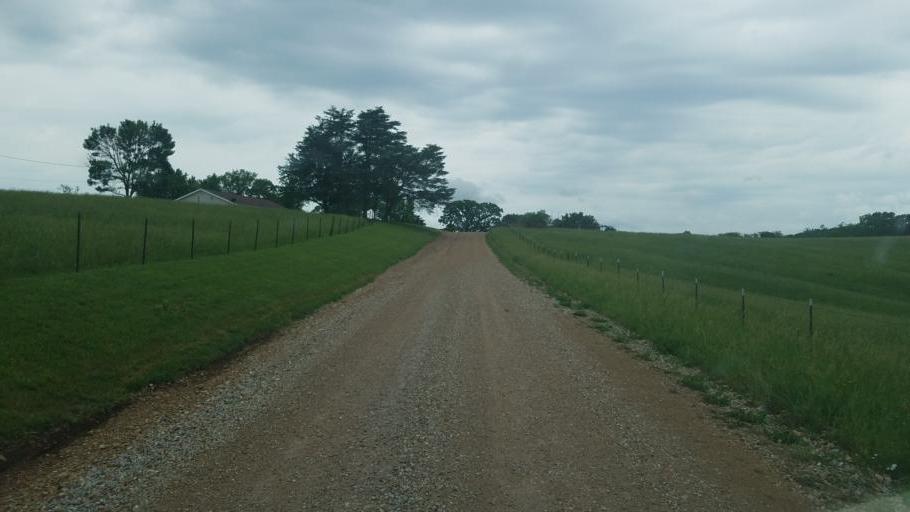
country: US
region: Missouri
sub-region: Moniteau County
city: California
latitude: 38.5918
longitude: -92.6589
